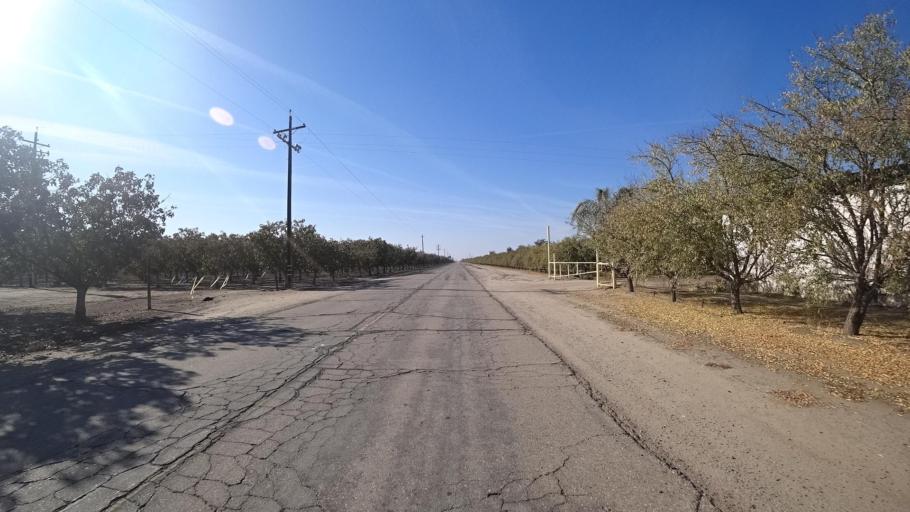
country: US
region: California
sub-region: Kern County
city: Wasco
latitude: 35.6669
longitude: -119.3526
